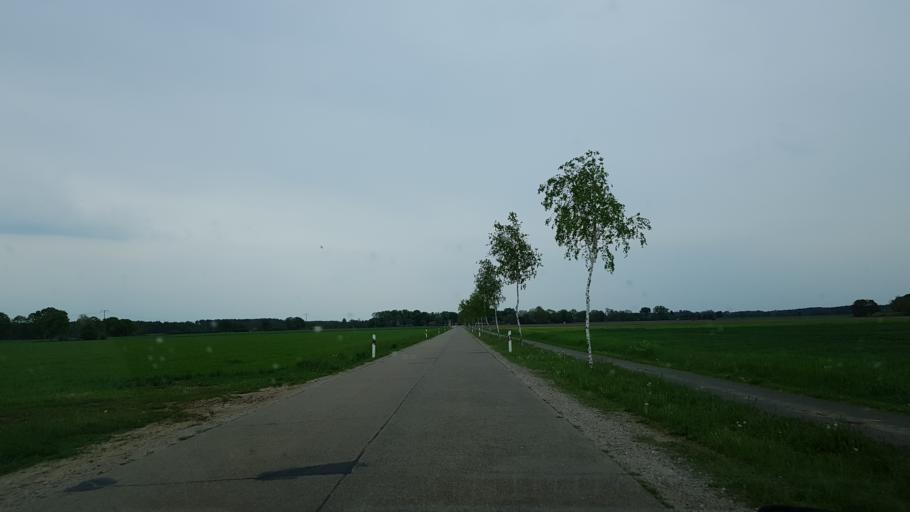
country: DE
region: Lower Saxony
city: Gartow
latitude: 53.0506
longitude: 11.4371
